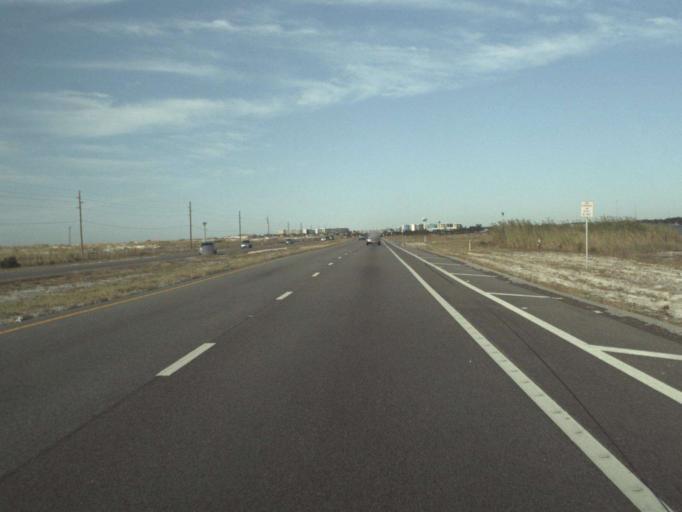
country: US
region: Florida
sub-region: Okaloosa County
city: Lake Lorraine
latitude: 30.3948
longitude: -86.5650
